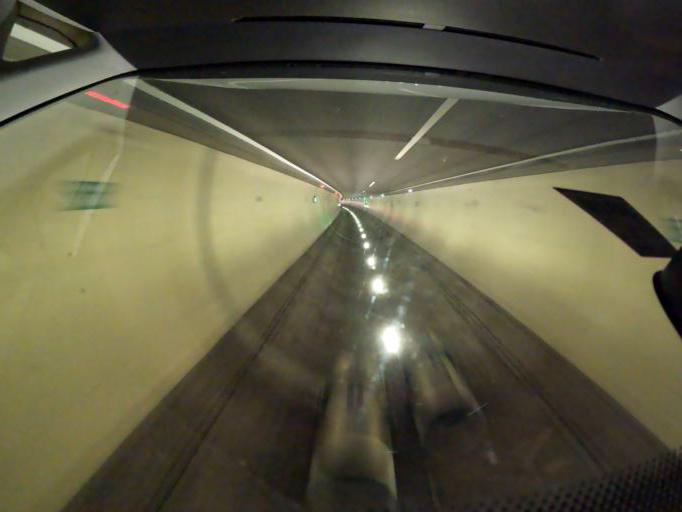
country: AT
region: Carinthia
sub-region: Politischer Bezirk Wolfsberg
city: Sankt Andrae
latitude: 46.7289
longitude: 14.8014
